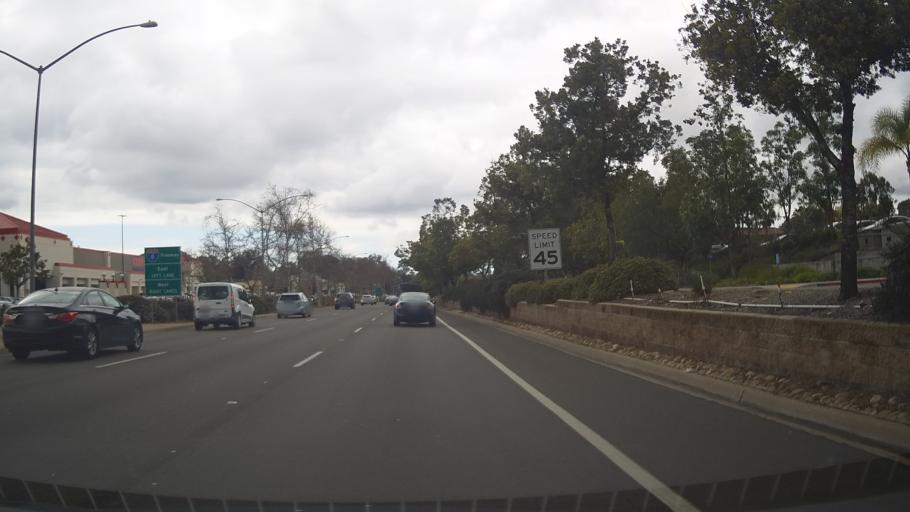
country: US
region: California
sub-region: San Diego County
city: La Mesa
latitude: 32.7752
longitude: -117.0236
